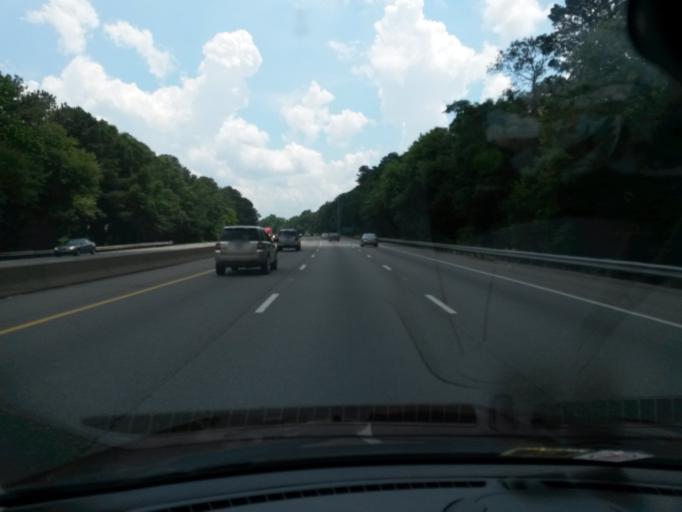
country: US
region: Virginia
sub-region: Chesterfield County
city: Bellwood
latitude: 37.3889
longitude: -77.4210
